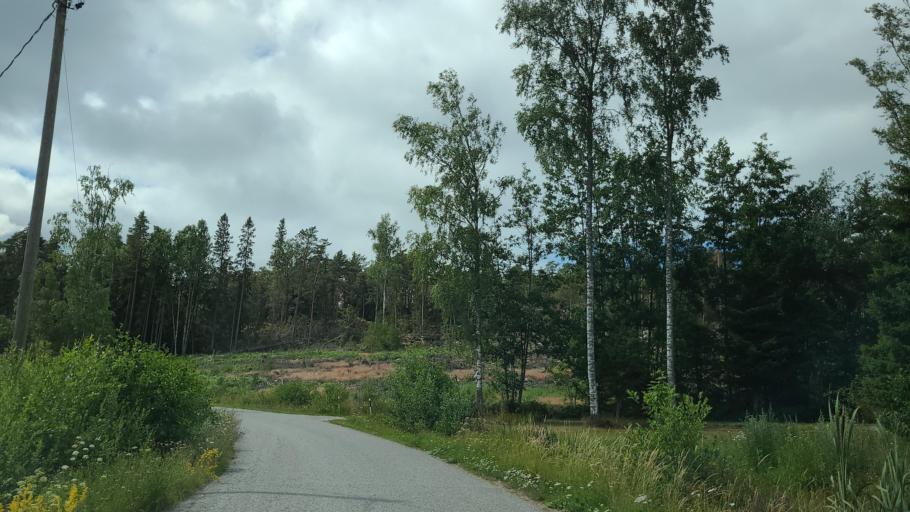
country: FI
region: Varsinais-Suomi
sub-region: Aboland-Turunmaa
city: Nagu
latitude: 60.1636
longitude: 22.0183
